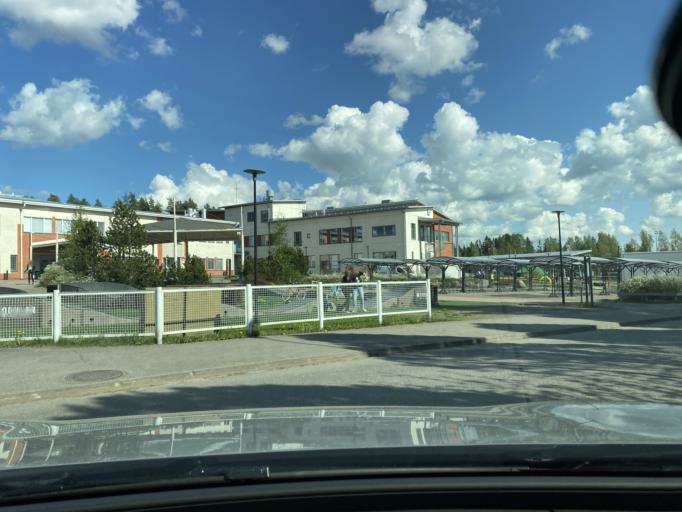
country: FI
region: Uusimaa
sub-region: Helsinki
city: Maentsaelae
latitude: 60.6473
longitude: 25.3170
